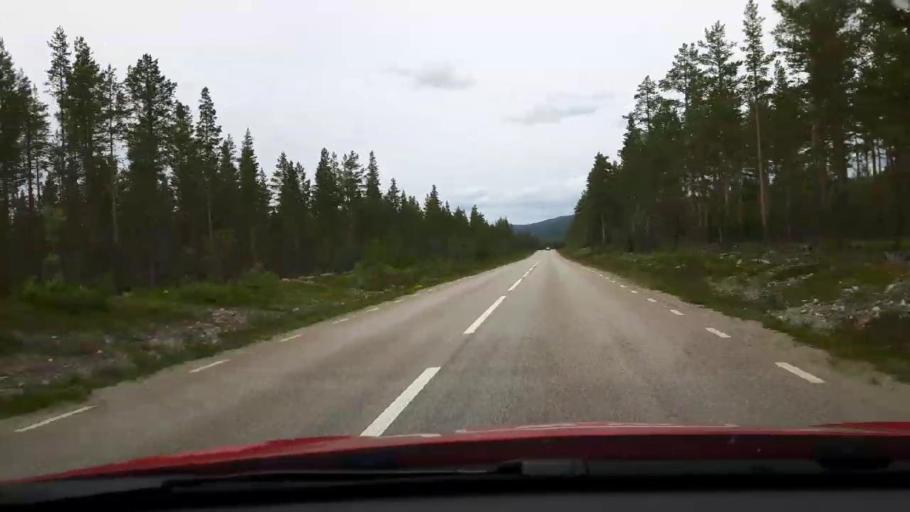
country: SE
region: Jaemtland
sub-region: Harjedalens Kommun
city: Sveg
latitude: 62.2524
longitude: 13.8414
